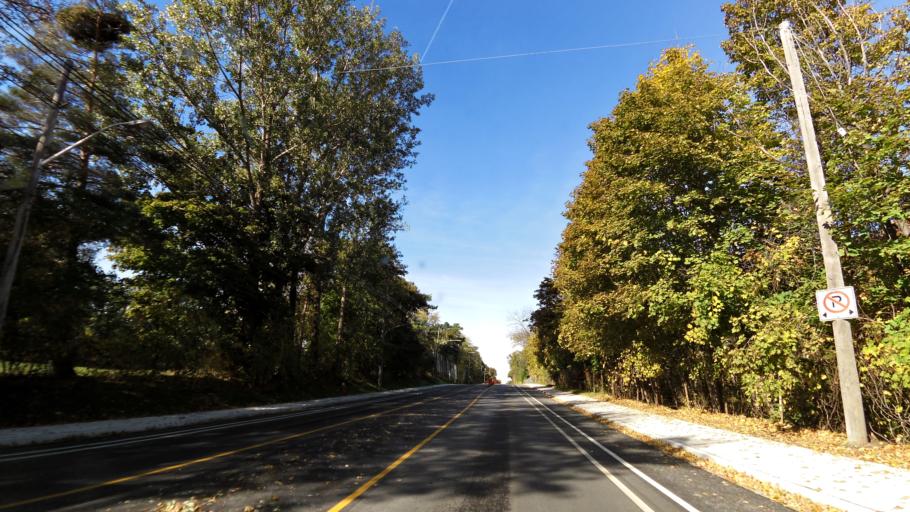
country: CA
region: Ontario
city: Etobicoke
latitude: 43.5880
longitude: -79.5561
